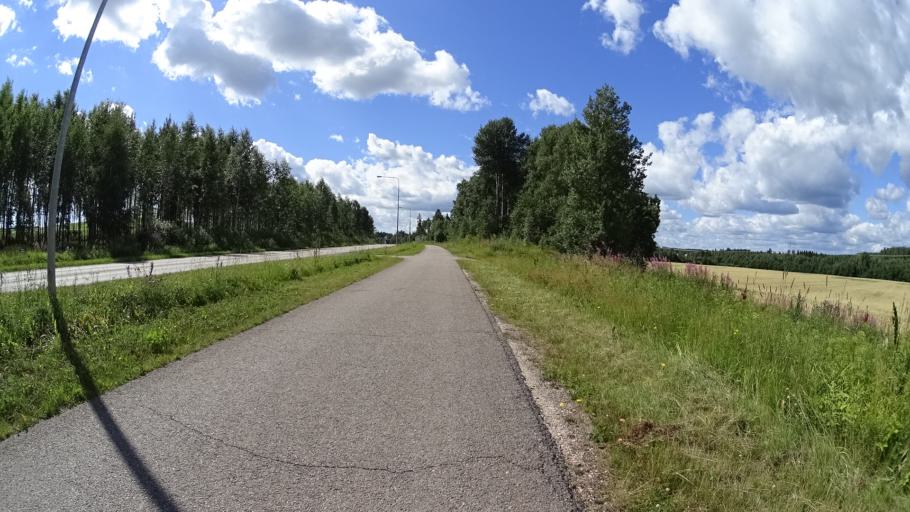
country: FI
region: Uusimaa
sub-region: Helsinki
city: Teekkarikylae
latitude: 60.3156
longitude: 24.8989
